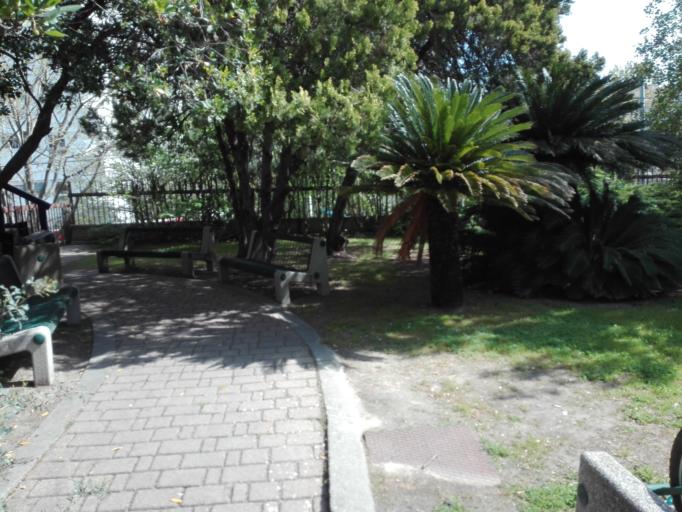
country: IT
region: Sardinia
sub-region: Provincia di Sassari
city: Sassari
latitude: 40.7169
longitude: 8.5541
